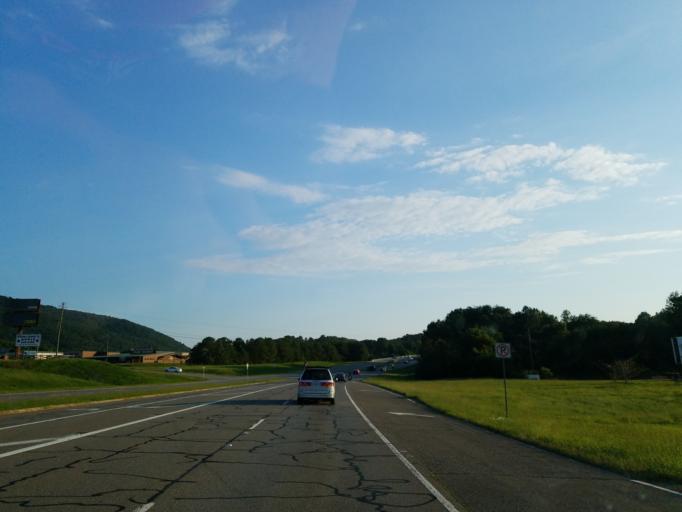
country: US
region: Georgia
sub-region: Gilmer County
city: Ellijay
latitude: 34.6434
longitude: -84.4970
